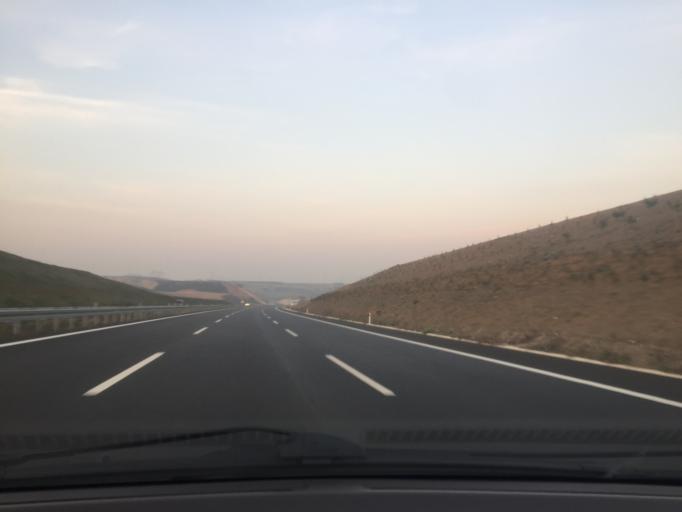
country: TR
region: Bursa
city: Mahmudiye
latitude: 40.2769
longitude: 28.5307
